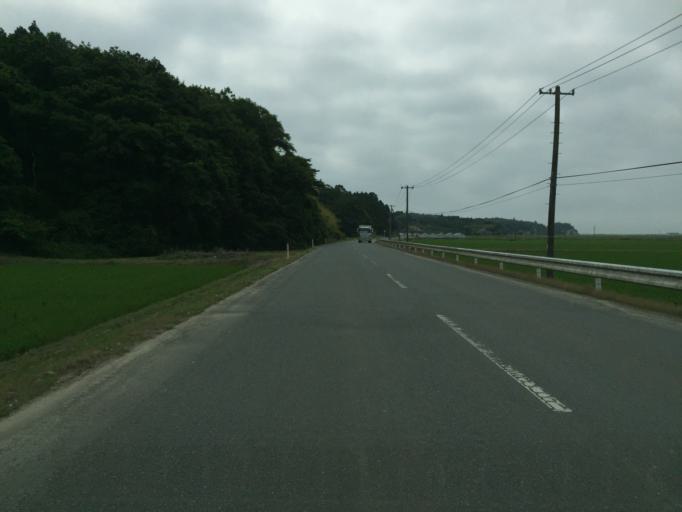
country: JP
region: Fukushima
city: Namie
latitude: 37.7410
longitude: 140.9855
